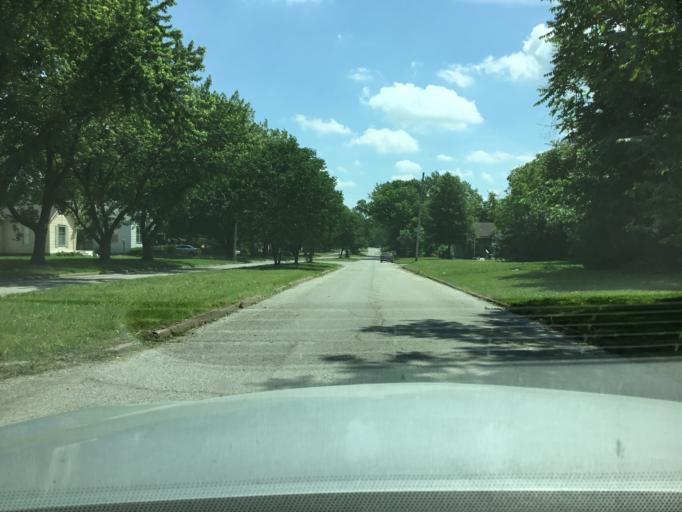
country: US
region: Kansas
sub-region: Labette County
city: Parsons
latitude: 37.3478
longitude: -95.2631
